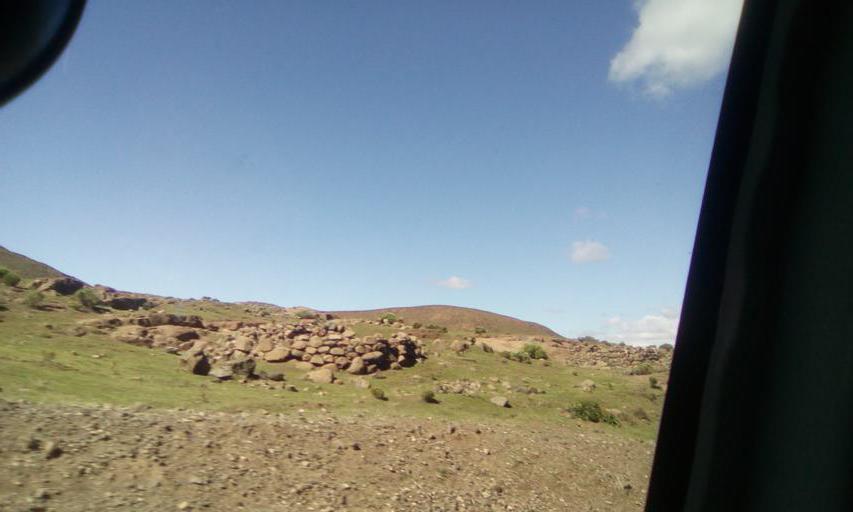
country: LS
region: Maseru
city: Nako
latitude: -29.8889
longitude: 28.1111
